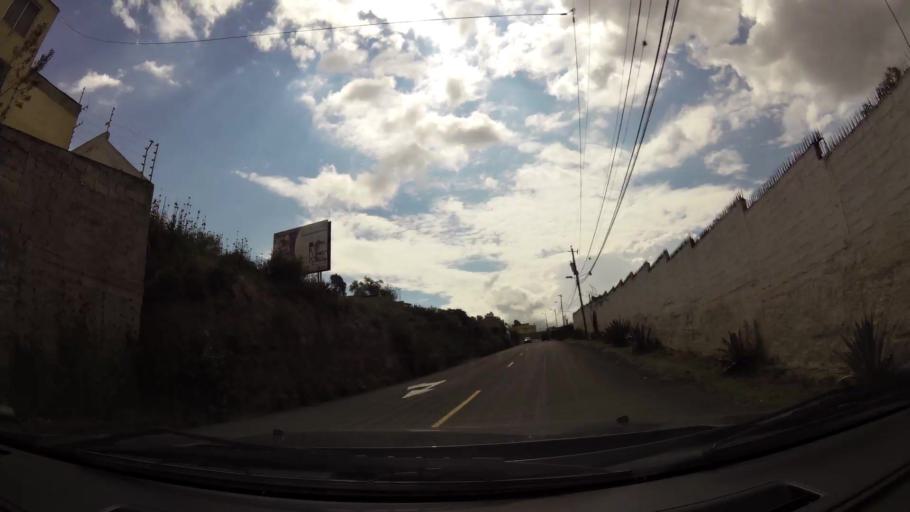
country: EC
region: Pichincha
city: Quito
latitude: -0.0977
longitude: -78.4629
